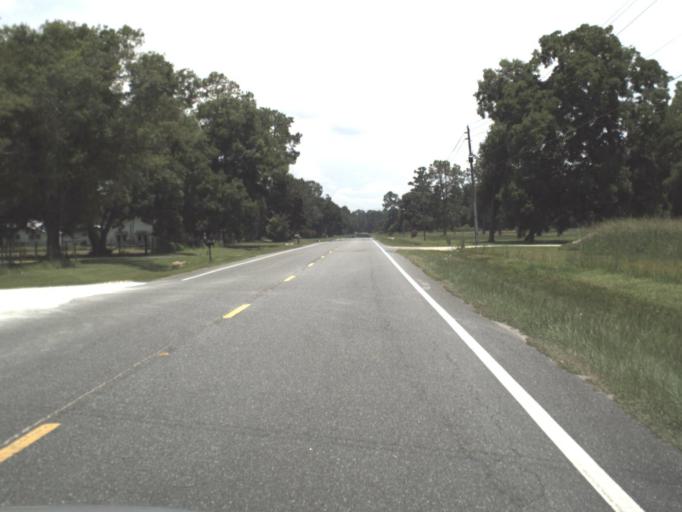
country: US
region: Florida
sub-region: Bradford County
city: Starke
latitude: 30.0347
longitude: -82.1622
